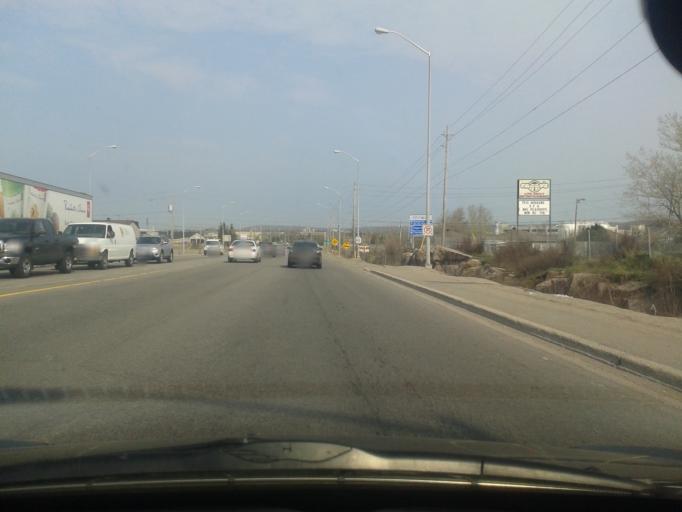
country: CA
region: Ontario
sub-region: Nipissing District
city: North Bay
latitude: 46.3096
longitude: -79.4386
